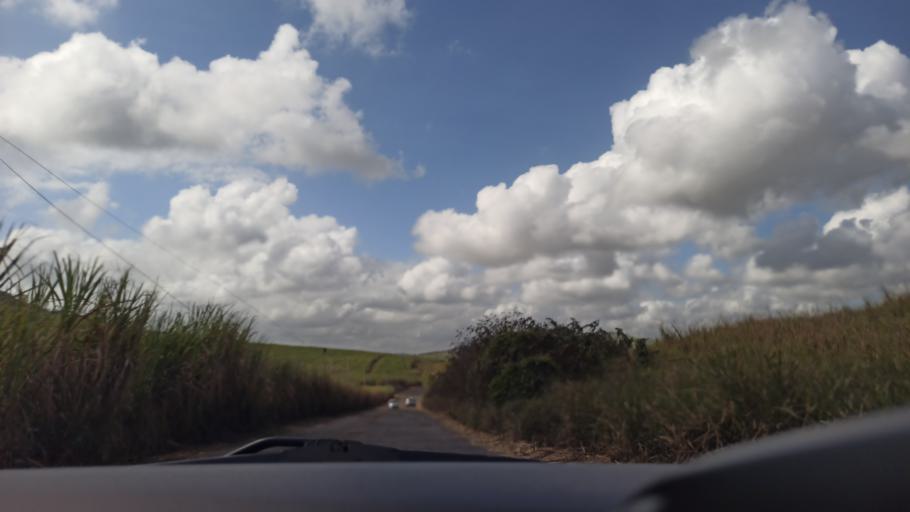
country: BR
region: Paraiba
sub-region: Juripiranga
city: Juripiranga
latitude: -7.4002
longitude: -35.2578
